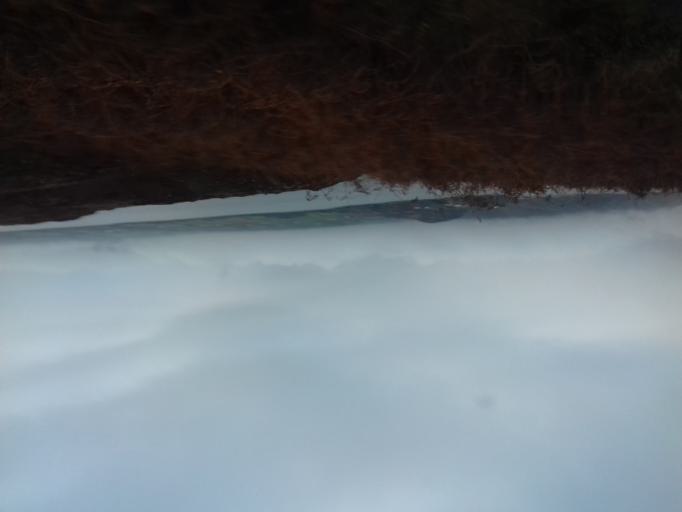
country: IE
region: Ulster
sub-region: County Donegal
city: Buncrana
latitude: 55.1824
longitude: -7.5868
